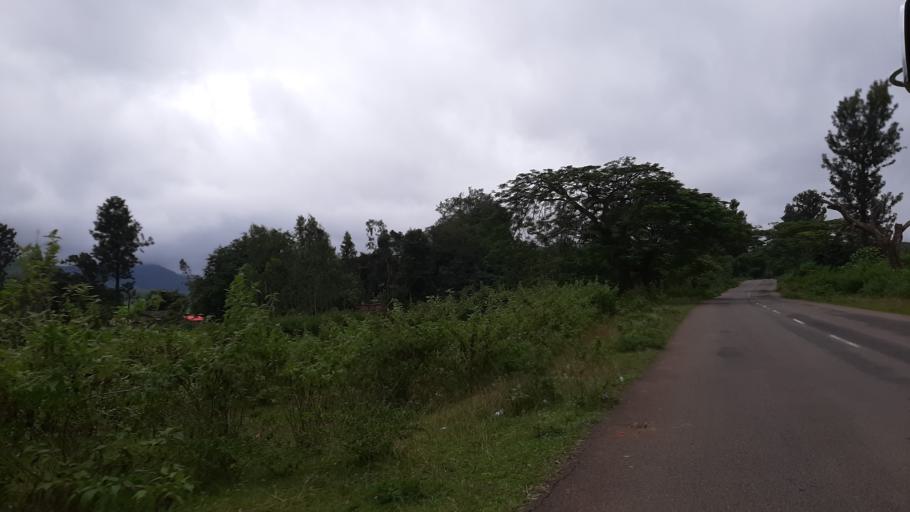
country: IN
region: Andhra Pradesh
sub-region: Vizianagaram District
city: Salur
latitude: 18.2998
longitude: 82.9116
